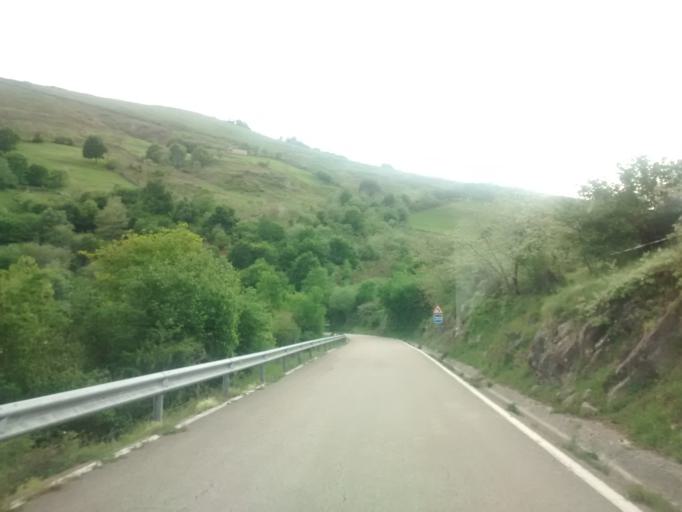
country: ES
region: Cantabria
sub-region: Provincia de Cantabria
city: San Vicente de la Barquera
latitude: 43.2558
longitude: -4.4418
